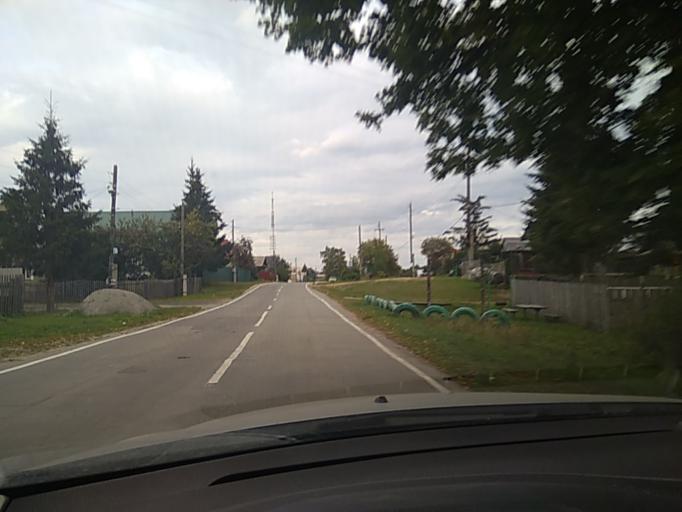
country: RU
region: Chelyabinsk
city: Kyshtym
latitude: 55.6941
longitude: 60.5378
